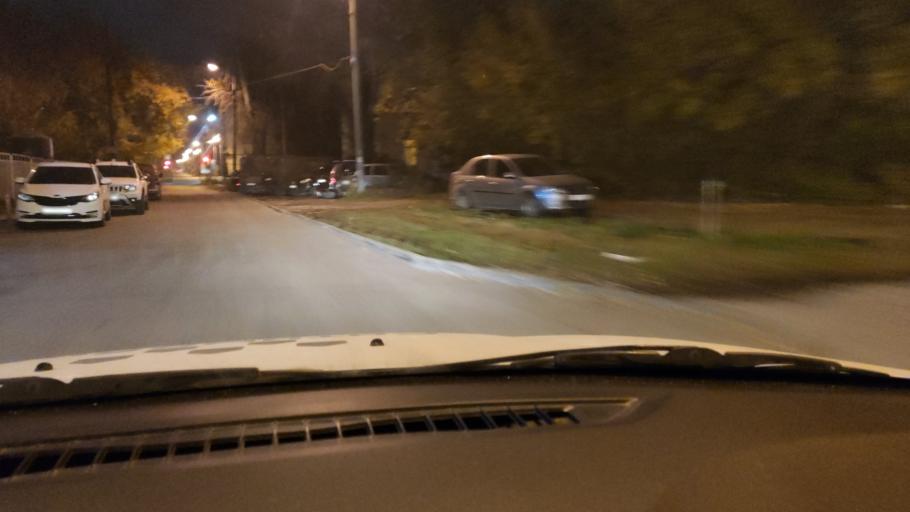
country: RU
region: Perm
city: Kondratovo
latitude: 58.0014
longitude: 56.1761
